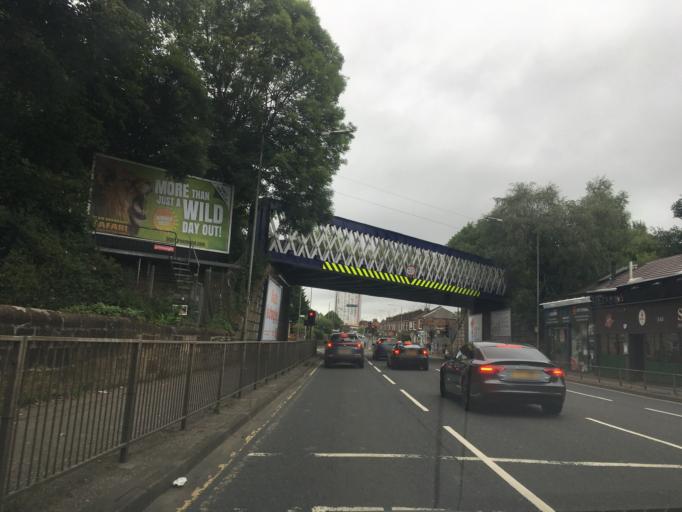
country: GB
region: Scotland
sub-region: East Dunbartonshire
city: Bearsden
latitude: 55.8828
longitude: -4.3261
